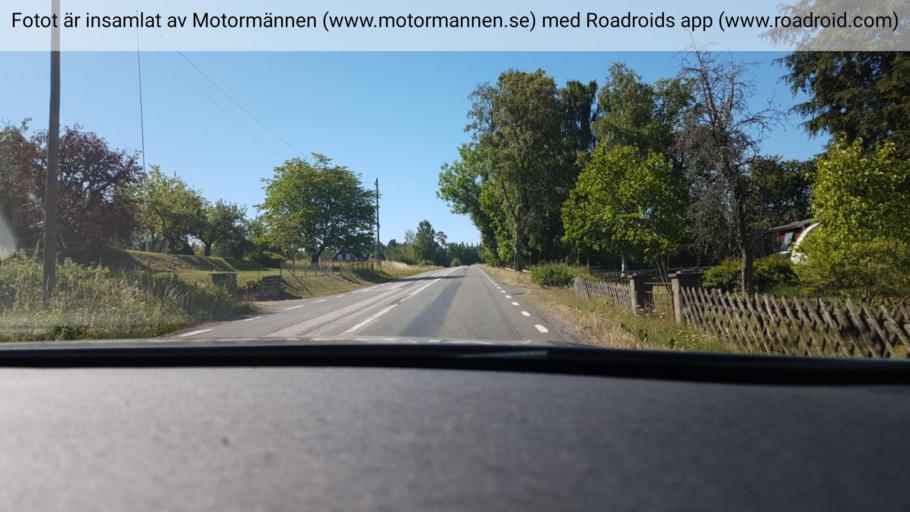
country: SE
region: Vaestra Goetaland
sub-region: Tidaholms Kommun
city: Tidaholm
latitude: 58.1530
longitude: 13.9650
